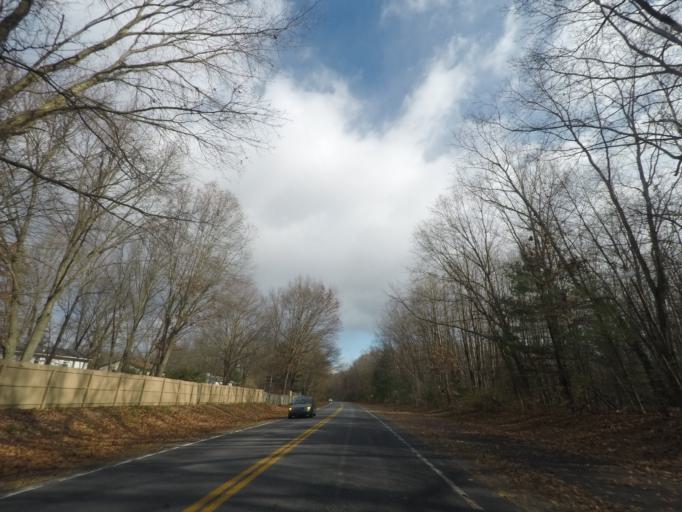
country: US
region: New York
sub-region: Saratoga County
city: Country Knolls
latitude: 42.8942
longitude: -73.8020
